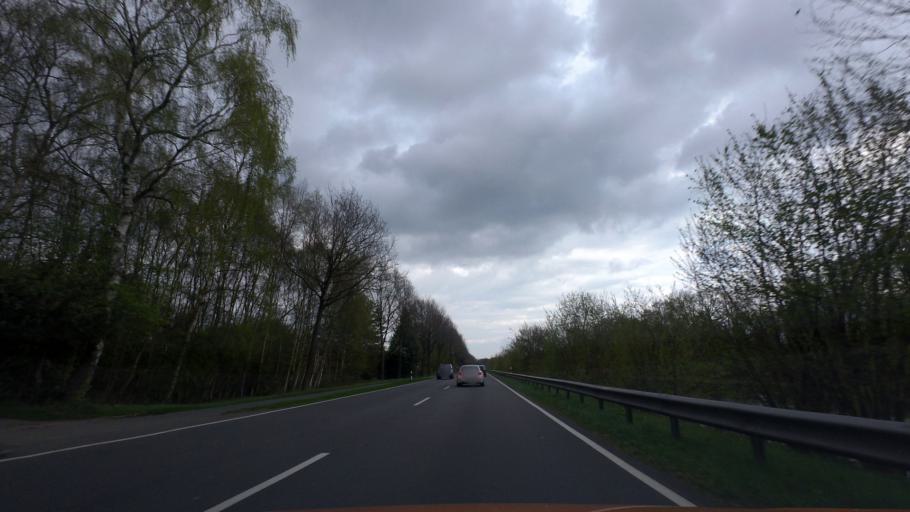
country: DE
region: Lower Saxony
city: Edewecht
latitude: 53.0846
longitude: 7.9797
